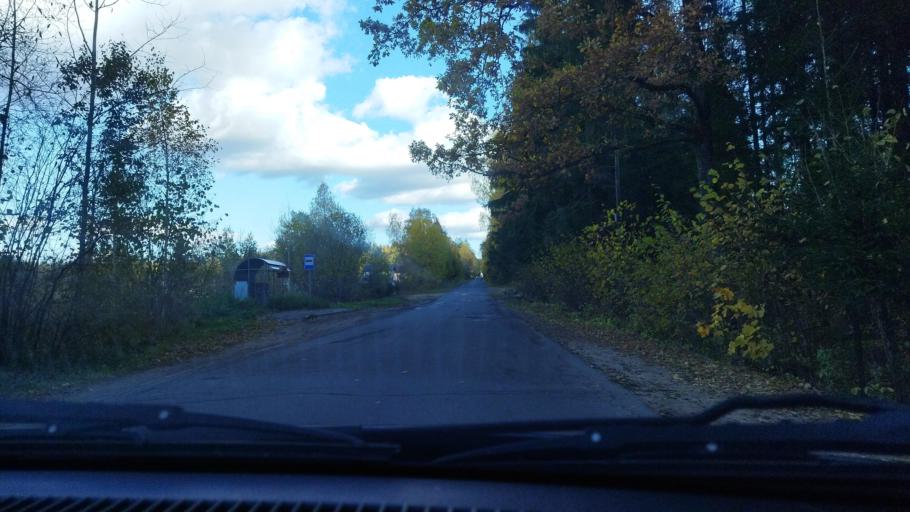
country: BY
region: Minsk
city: Slabada
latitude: 53.9829
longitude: 27.8769
